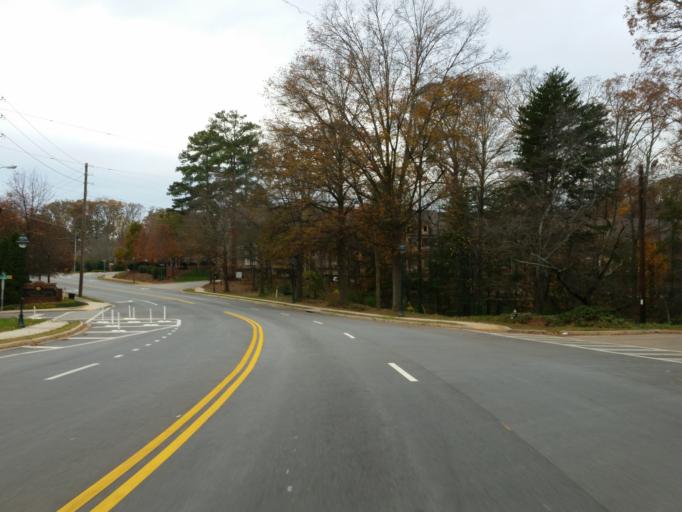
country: US
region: Georgia
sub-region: Fulton County
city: Sandy Springs
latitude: 33.9070
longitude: -84.3663
